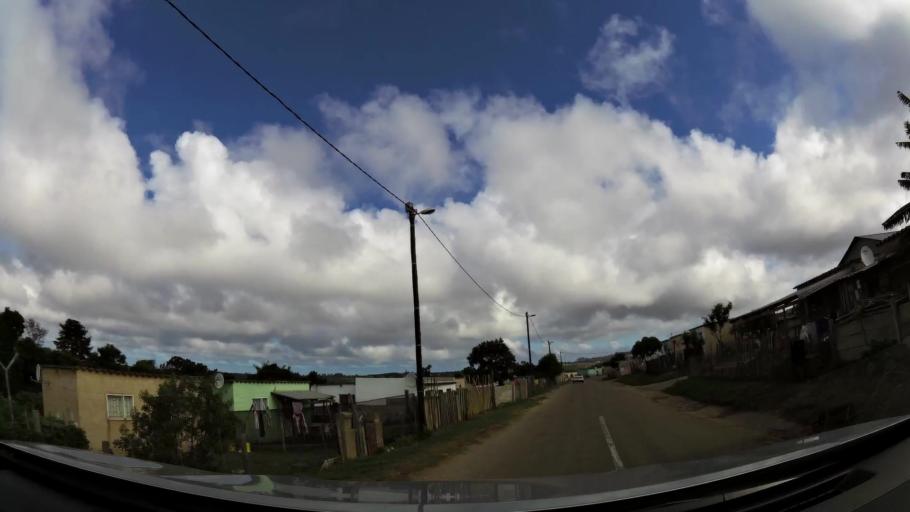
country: ZA
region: Western Cape
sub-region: Eden District Municipality
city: Plettenberg Bay
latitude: -34.0551
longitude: 23.3124
